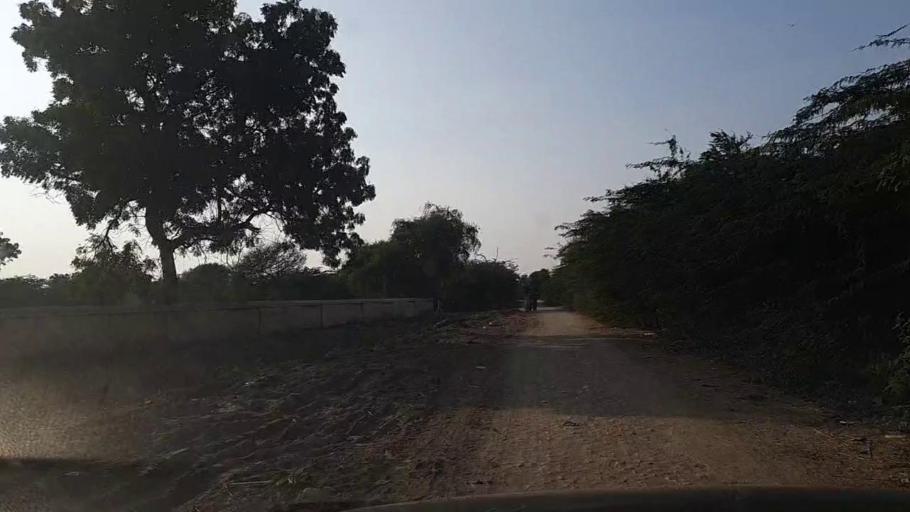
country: PK
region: Sindh
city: Gharo
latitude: 24.7779
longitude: 67.5082
